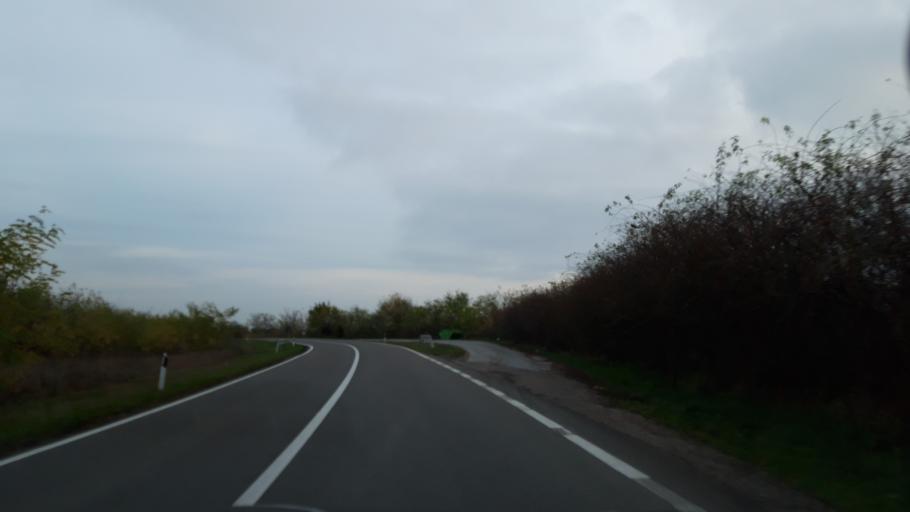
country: RS
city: Sanad
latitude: 45.9662
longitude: 20.1260
